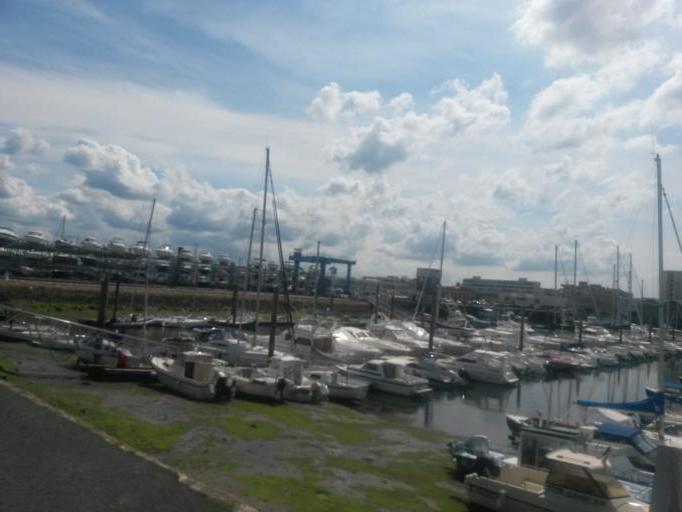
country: FR
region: Aquitaine
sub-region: Departement de la Gironde
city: Arcachon
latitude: 44.6601
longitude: -1.1447
